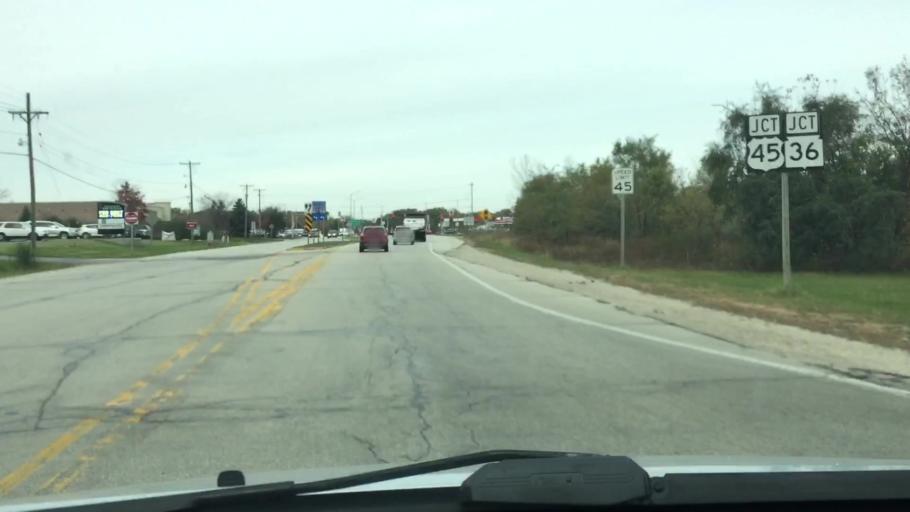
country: US
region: Wisconsin
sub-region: Milwaukee County
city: Franklin
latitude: 42.8872
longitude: -88.0361
